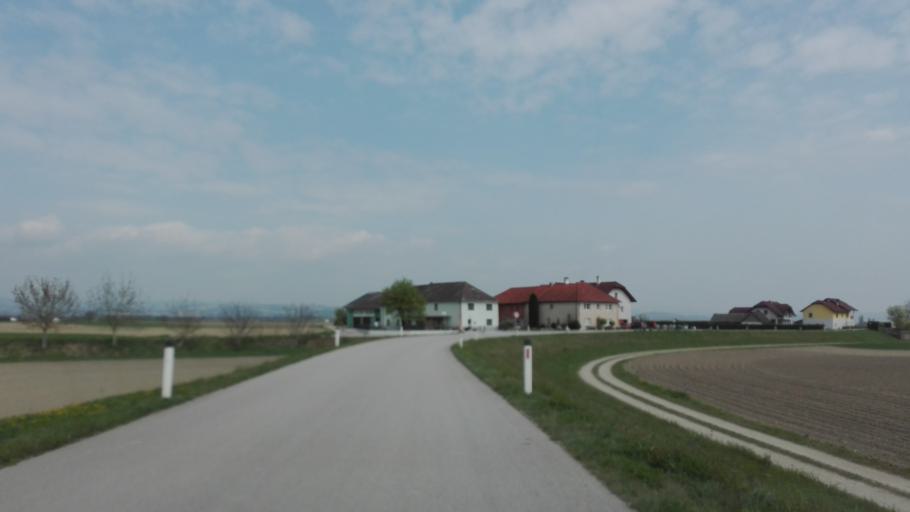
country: AT
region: Lower Austria
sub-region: Politischer Bezirk Amstetten
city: Strengberg
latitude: 48.1818
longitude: 14.6527
